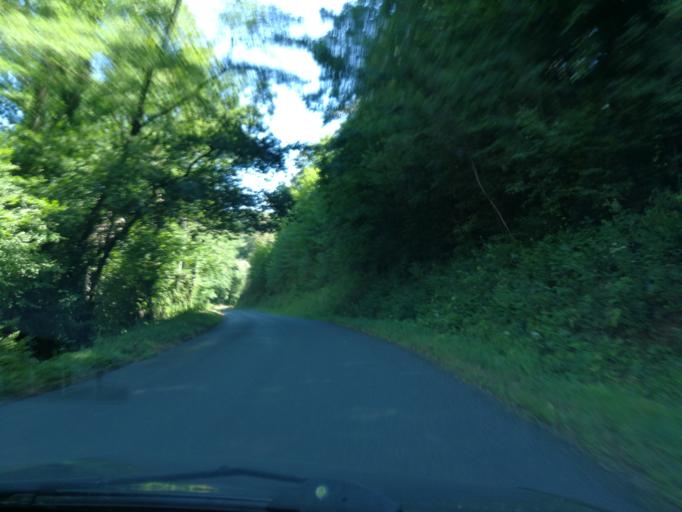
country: FR
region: Limousin
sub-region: Departement de la Correze
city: Argentat
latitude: 45.0935
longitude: 1.9166
